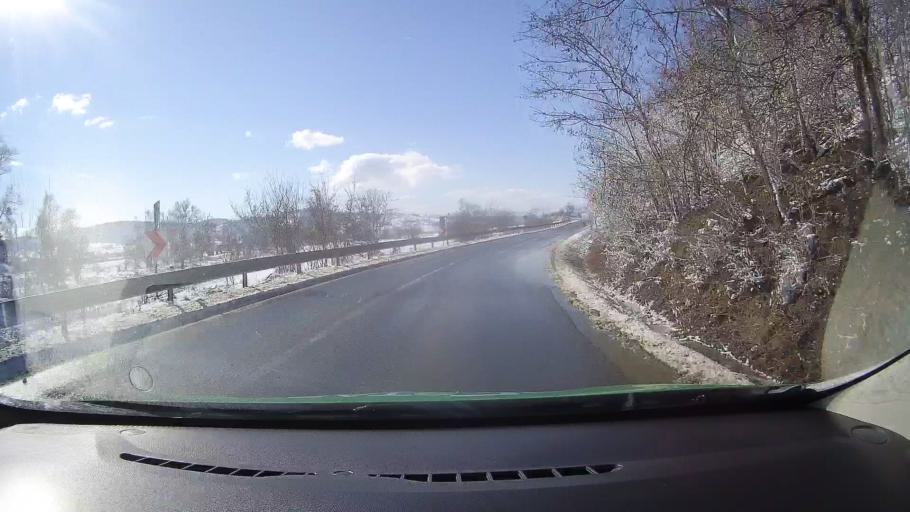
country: RO
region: Sibiu
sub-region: Comuna Rosia
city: Rosia
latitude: 45.8016
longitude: 24.3518
